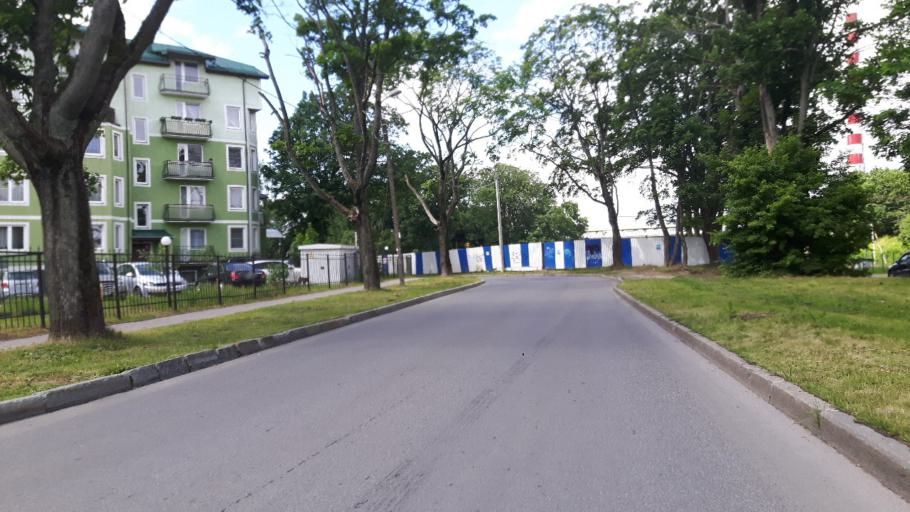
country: RU
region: Kaliningrad
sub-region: Gorod Kaliningrad
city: Kaliningrad
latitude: 54.7344
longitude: 20.5126
